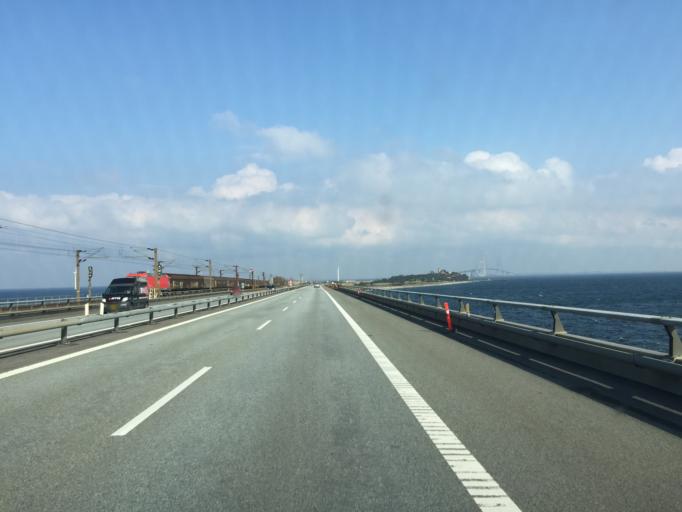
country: DK
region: South Denmark
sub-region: Nyborg Kommune
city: Nyborg
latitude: 55.3245
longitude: 10.9442
